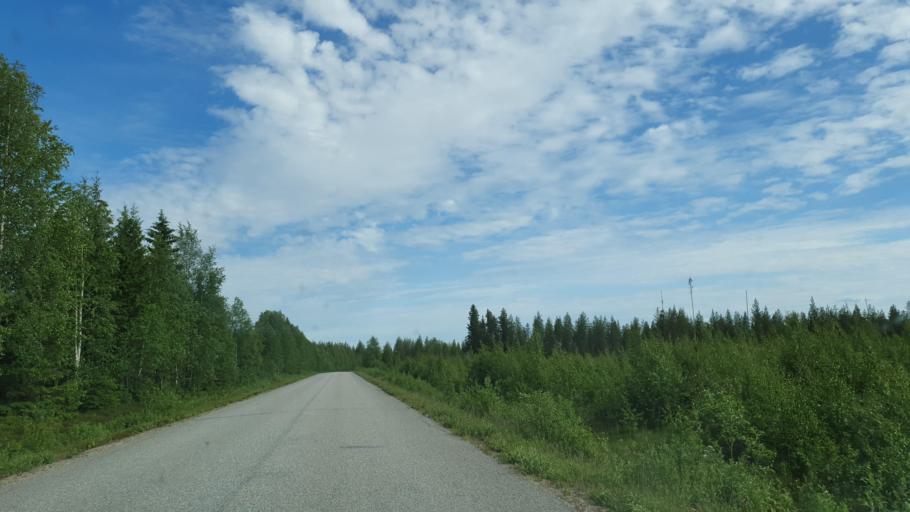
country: FI
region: Kainuu
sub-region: Kehys-Kainuu
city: Suomussalmi
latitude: 64.5491
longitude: 29.2371
